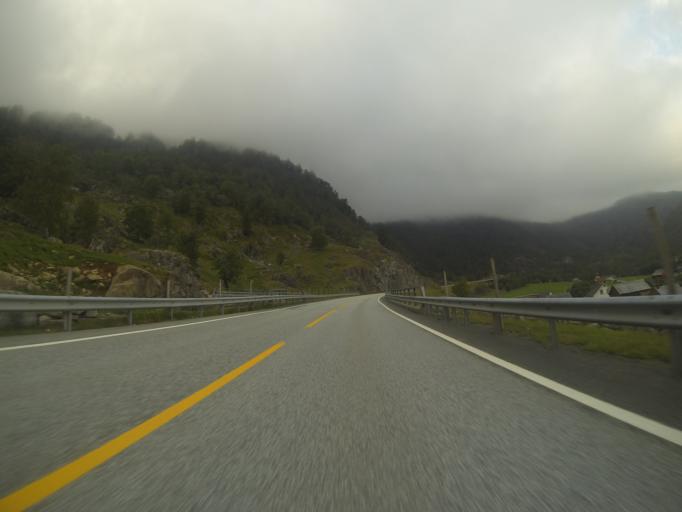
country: NO
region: Hordaland
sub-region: Odda
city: Odda
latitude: 59.8781
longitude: 6.4251
